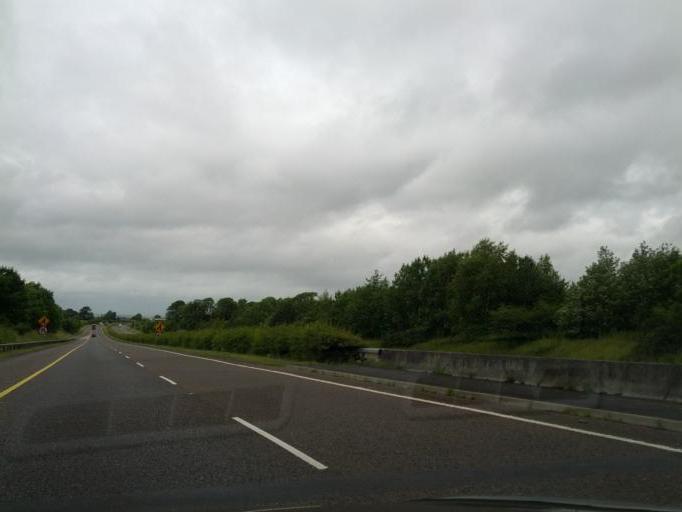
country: IE
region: Munster
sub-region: An Clar
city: Newmarket on Fergus
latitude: 52.7523
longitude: -8.9035
